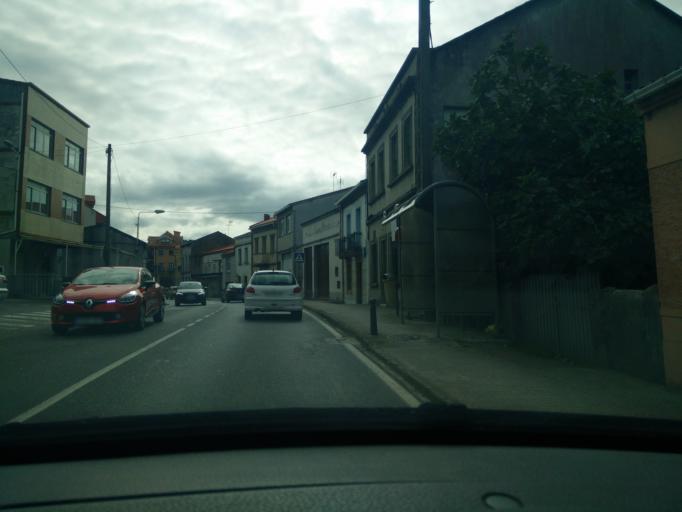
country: ES
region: Galicia
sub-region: Provincia da Coruna
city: A Coruna
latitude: 43.3332
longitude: -8.4241
